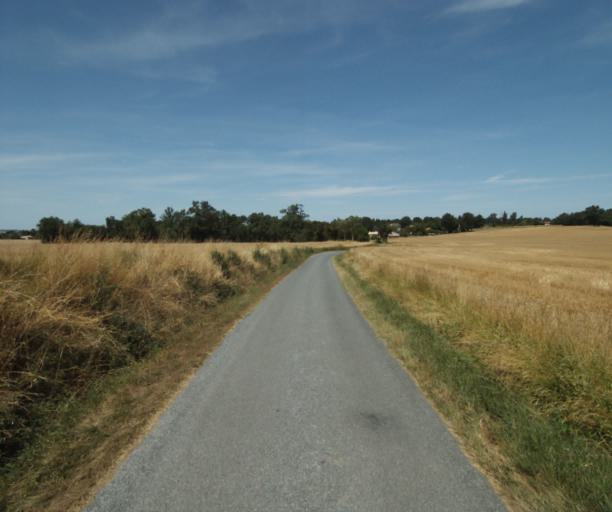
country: FR
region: Midi-Pyrenees
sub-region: Departement du Tarn
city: Soreze
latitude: 43.4861
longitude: 2.0570
